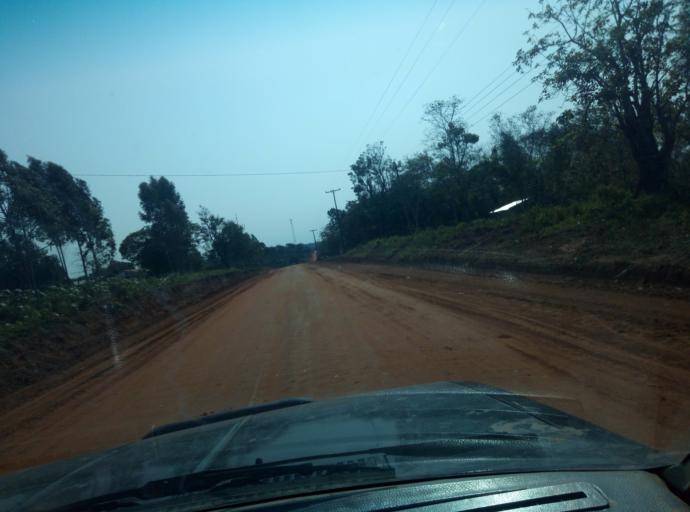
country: PY
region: Caaguazu
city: Carayao
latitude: -25.3225
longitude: -56.3294
